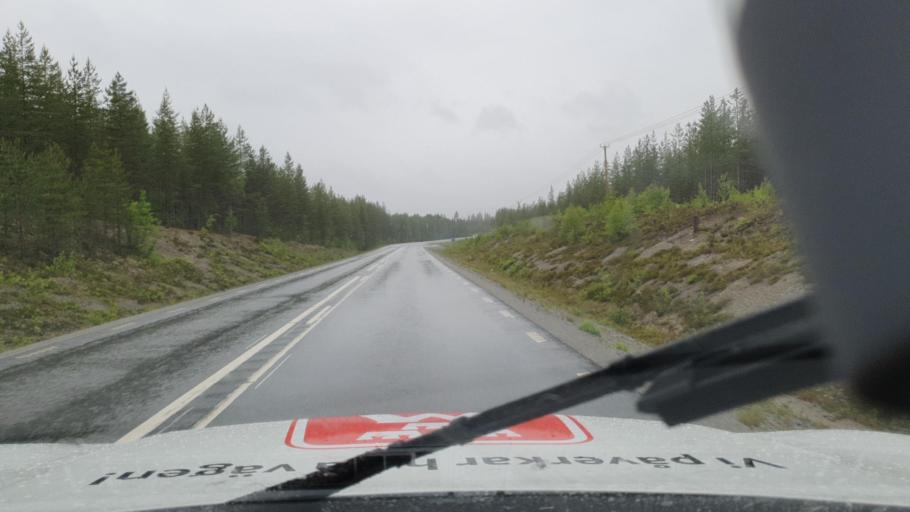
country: SE
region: Vaesterbotten
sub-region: Asele Kommun
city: Insjon
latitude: 64.1312
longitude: 18.0597
